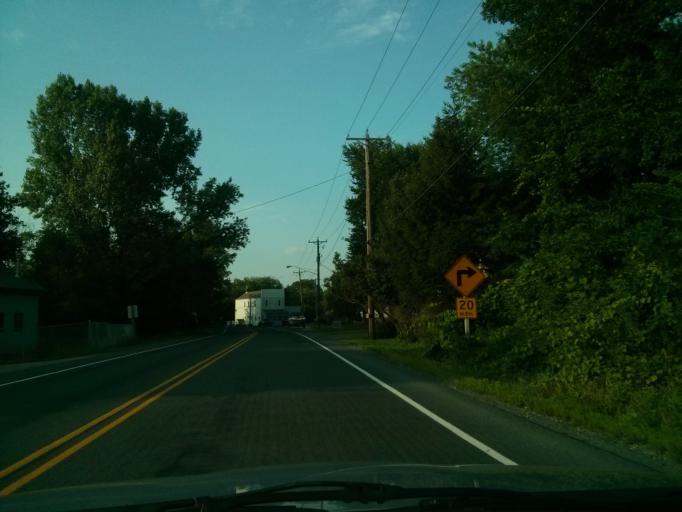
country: US
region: Wisconsin
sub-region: Saint Croix County
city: North Hudson
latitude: 45.0203
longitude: -92.6683
